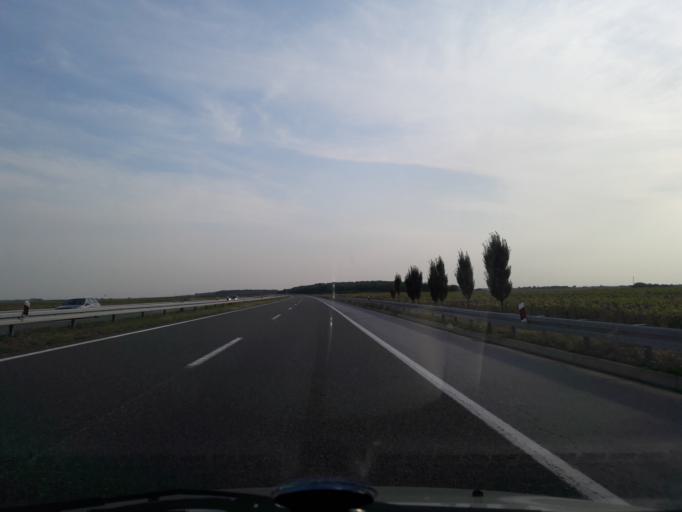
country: HR
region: Osjecko-Baranjska
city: Cepin
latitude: 45.5293
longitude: 18.5154
